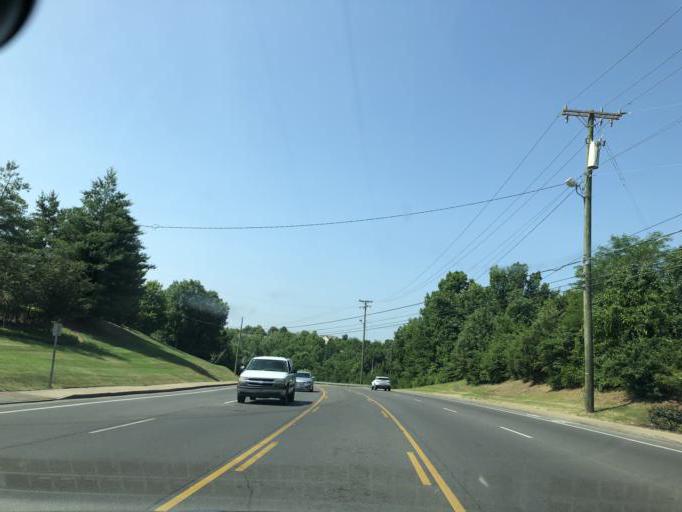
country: US
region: Tennessee
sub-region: Rutherford County
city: La Vergne
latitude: 36.0597
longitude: -86.6409
